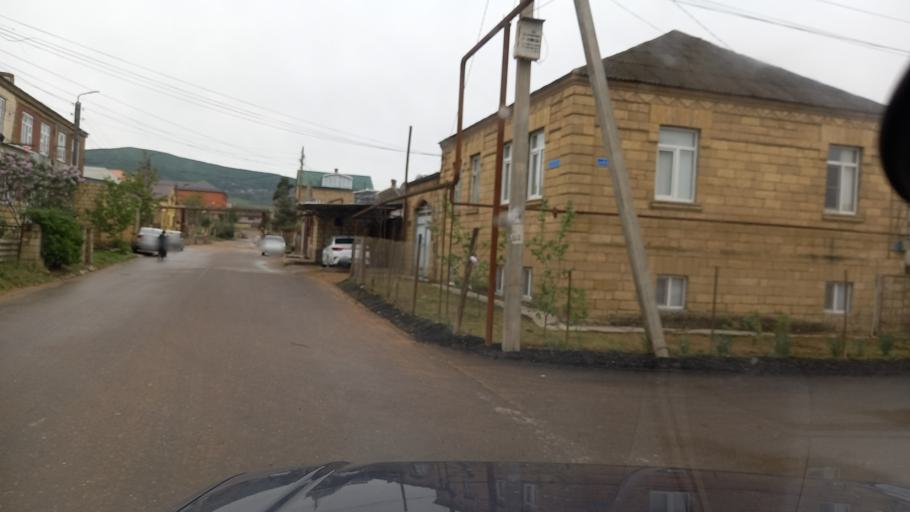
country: RU
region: Dagestan
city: Derbent
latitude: 42.0802
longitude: 48.2946
